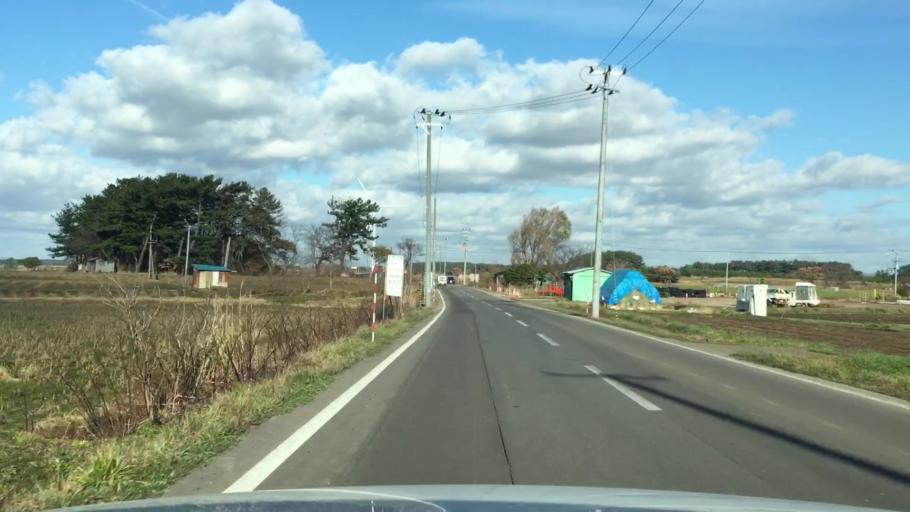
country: JP
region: Aomori
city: Shimokizukuri
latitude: 40.8548
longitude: 140.3018
